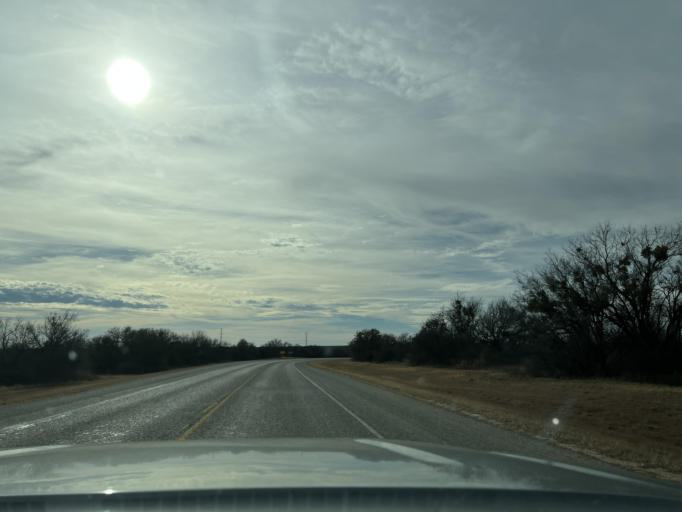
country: US
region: Texas
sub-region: Jones County
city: Stamford
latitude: 32.7589
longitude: -99.6049
